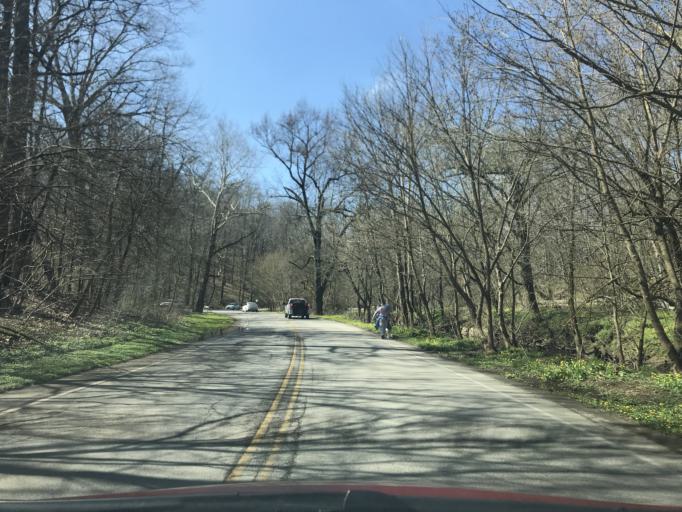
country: US
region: Kentucky
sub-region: Jefferson County
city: Saint Matthews
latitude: 38.2379
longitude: -85.6890
